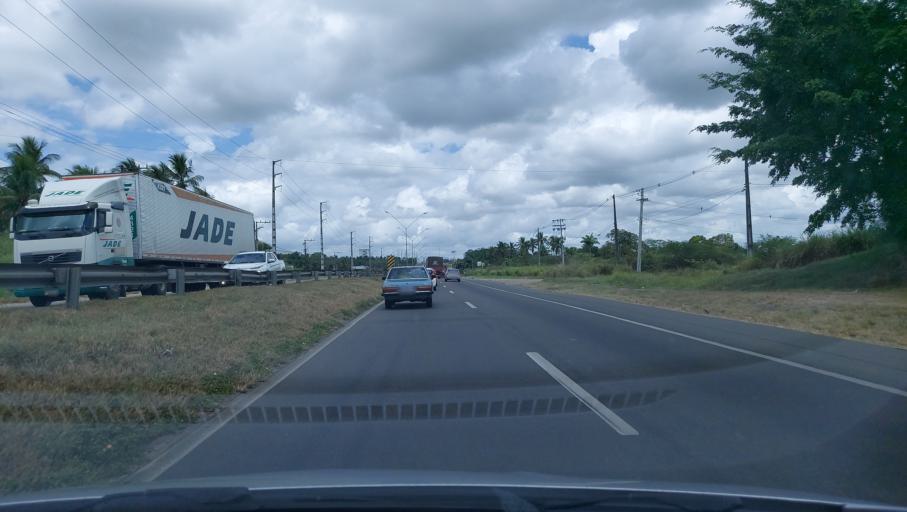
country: BR
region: Bahia
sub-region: Conceicao Do Jacuipe
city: Conceicao do Jacuipe
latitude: -12.3266
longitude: -38.8637
